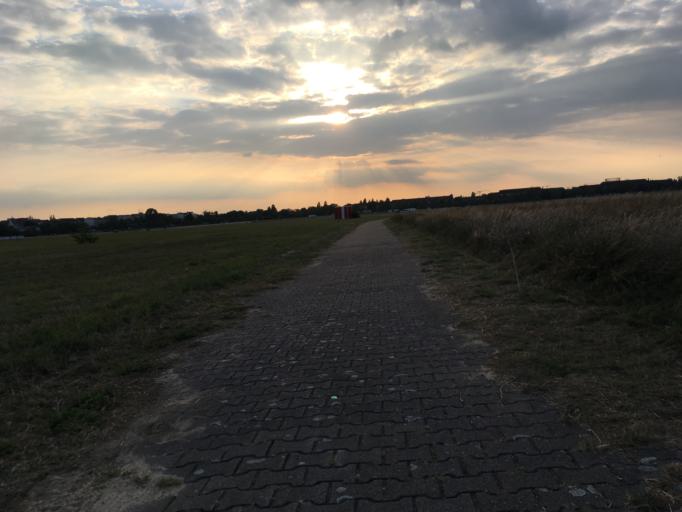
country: DE
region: Berlin
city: Tempelhof Bezirk
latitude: 52.4724
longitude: 13.3995
